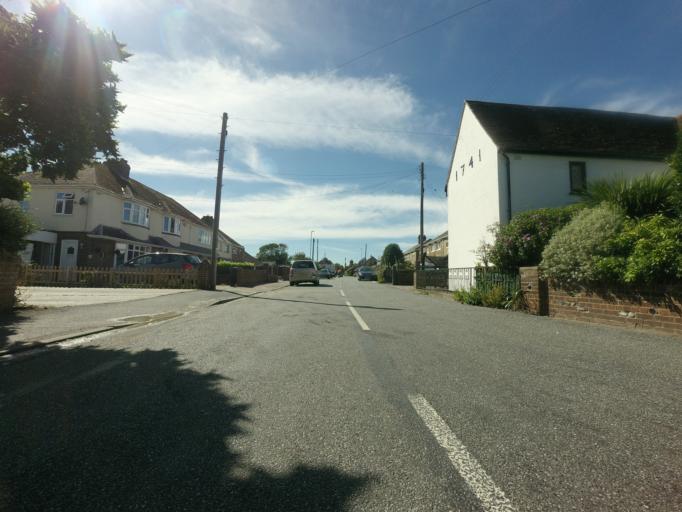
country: GB
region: England
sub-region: Kent
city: Birchington-on-Sea
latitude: 51.3391
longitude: 1.2807
